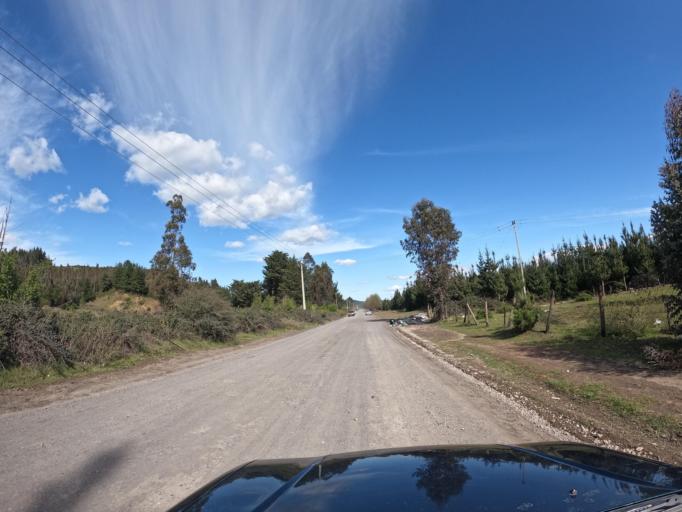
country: CL
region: Biobio
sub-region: Provincia de Concepcion
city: Chiguayante
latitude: -37.0673
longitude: -72.9467
